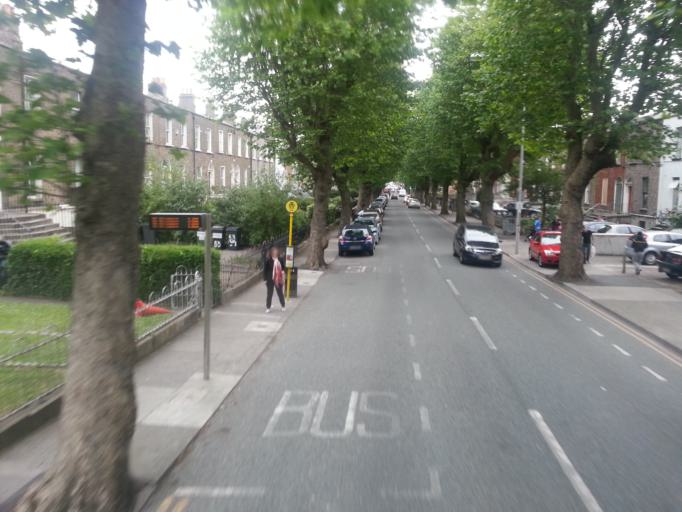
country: IE
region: Leinster
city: Cabra
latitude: 53.3539
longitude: -6.2955
